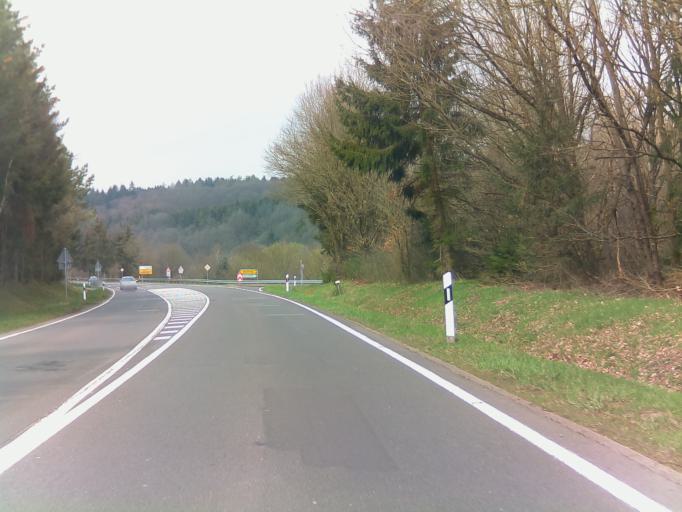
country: DE
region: Rheinland-Pfalz
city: Asbach
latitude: 49.8040
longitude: 7.2773
